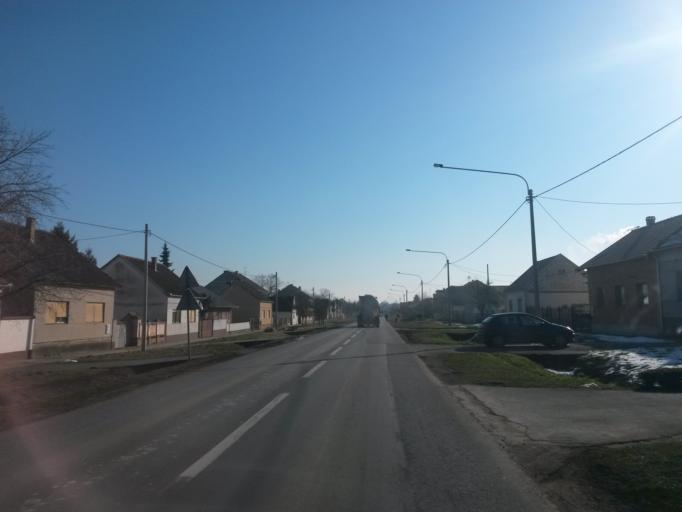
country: HR
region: Osjecko-Baranjska
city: Sarvas
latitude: 45.5172
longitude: 18.8752
